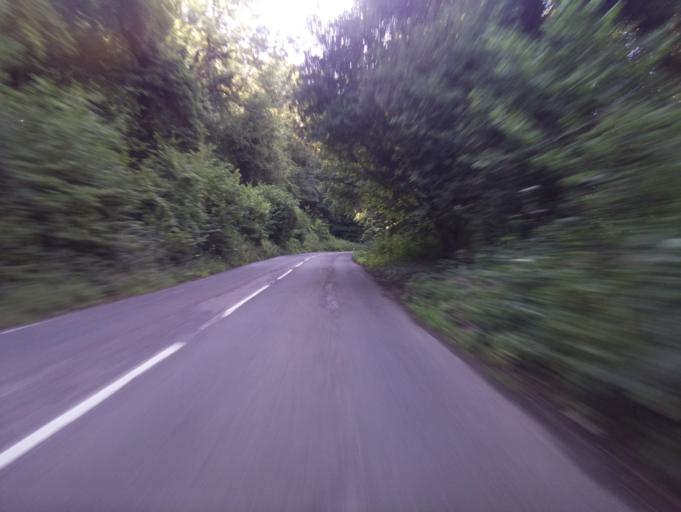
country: GB
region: England
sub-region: Gloucestershire
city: Lydbrook
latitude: 51.8505
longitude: -2.5954
